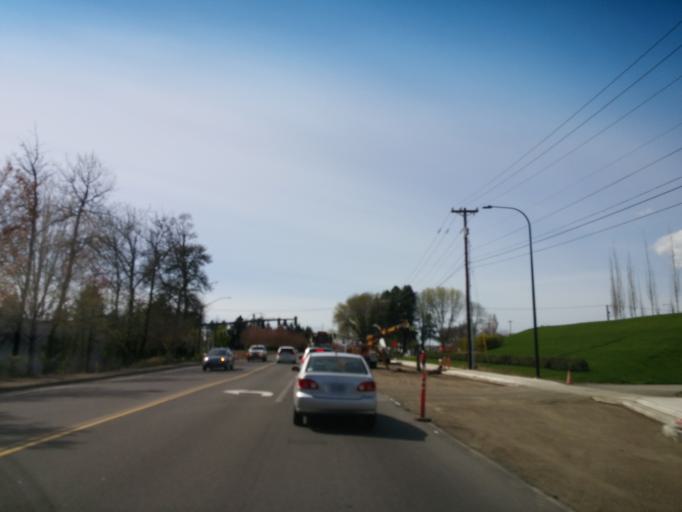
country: US
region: Oregon
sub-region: Washington County
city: Aloha
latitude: 45.5072
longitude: -122.8391
